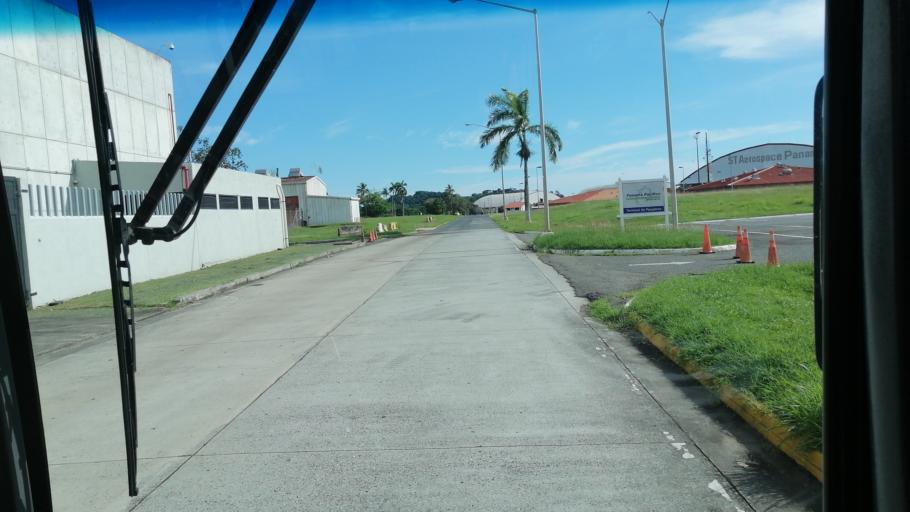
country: PA
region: Panama
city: Veracruz
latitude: 8.9200
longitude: -79.5944
